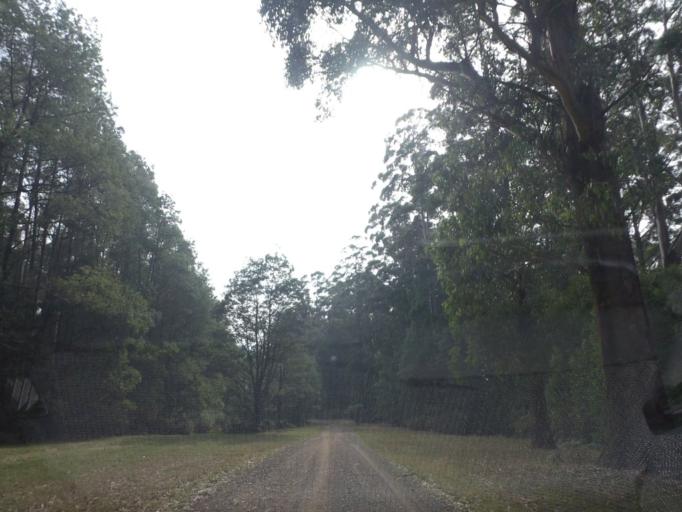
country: AU
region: Victoria
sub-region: Yarra Ranges
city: Healesville
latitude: -37.5926
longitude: 145.5635
